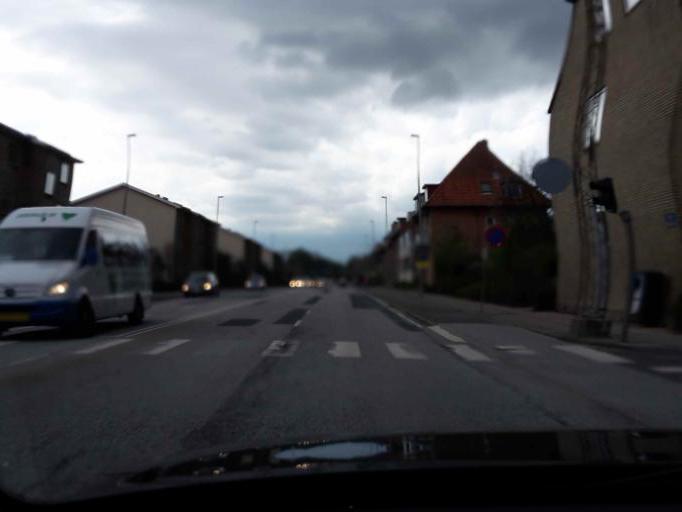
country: DK
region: South Denmark
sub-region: Odense Kommune
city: Odense
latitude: 55.3818
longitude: 10.4032
